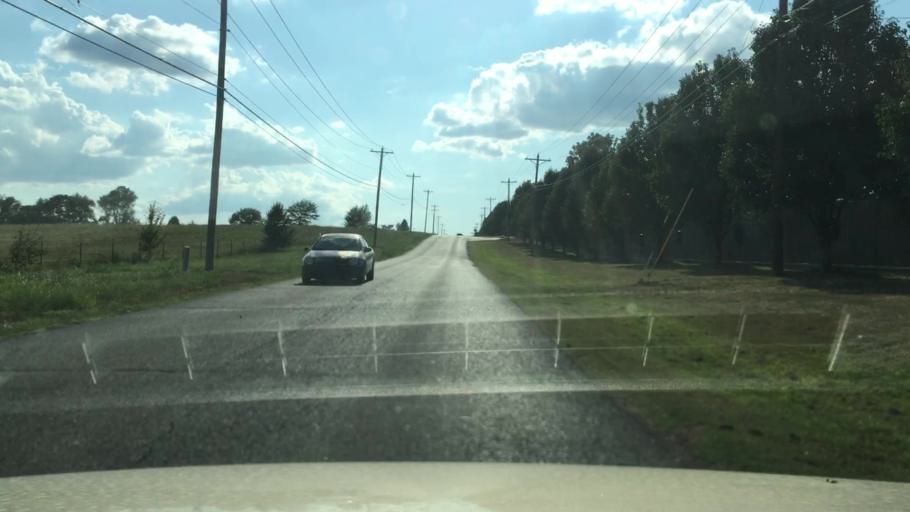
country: US
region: Oklahoma
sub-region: Cherokee County
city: Tahlequah
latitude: 35.9299
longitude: -94.9792
